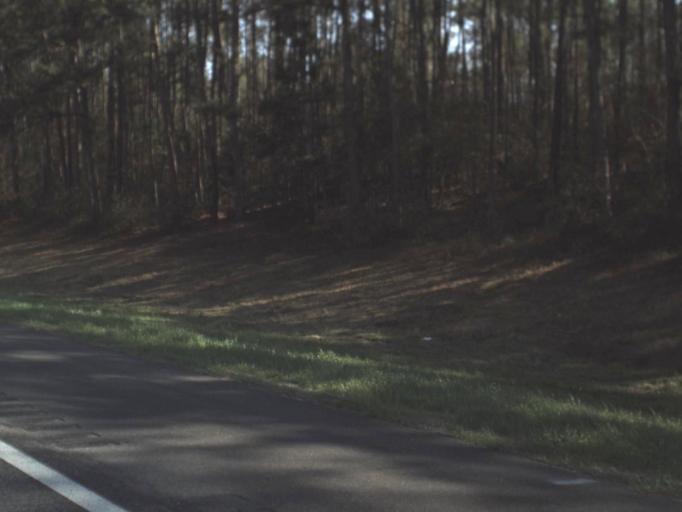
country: US
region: Florida
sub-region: Gadsden County
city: Quincy
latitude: 30.5333
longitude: -84.5785
